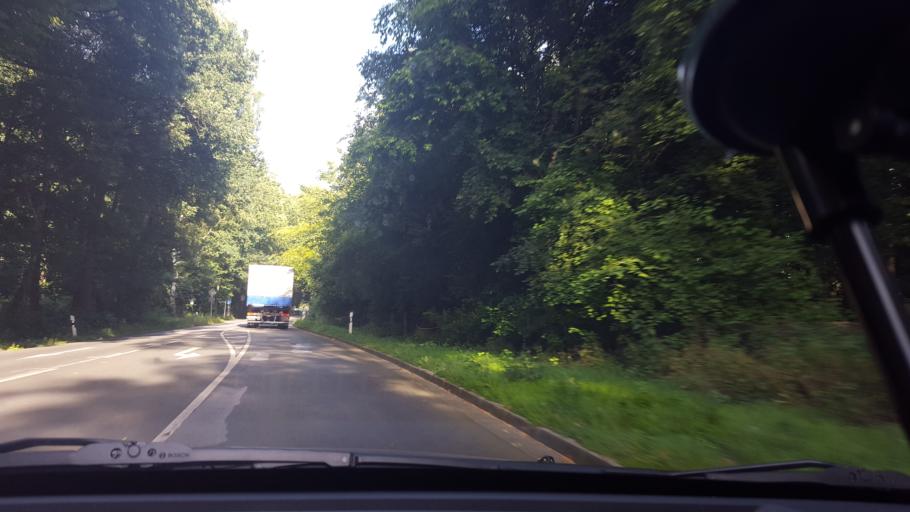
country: DE
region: North Rhine-Westphalia
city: Marl
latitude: 51.6600
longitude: 7.0421
